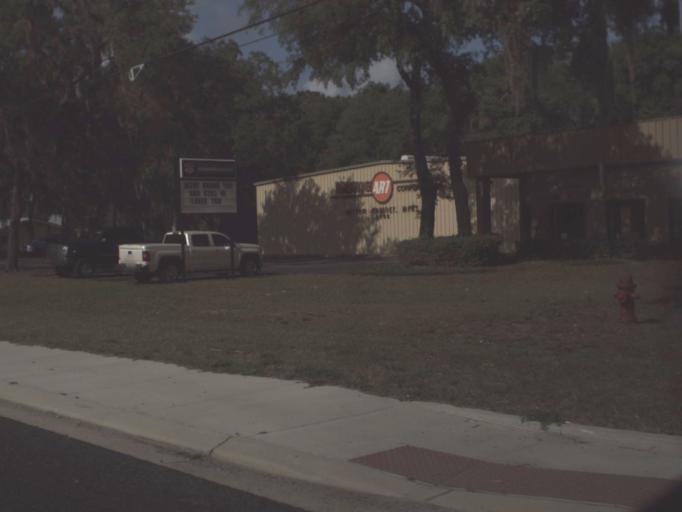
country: US
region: Florida
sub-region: Lake County
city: Fruitland Park
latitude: 28.8751
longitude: -81.9066
